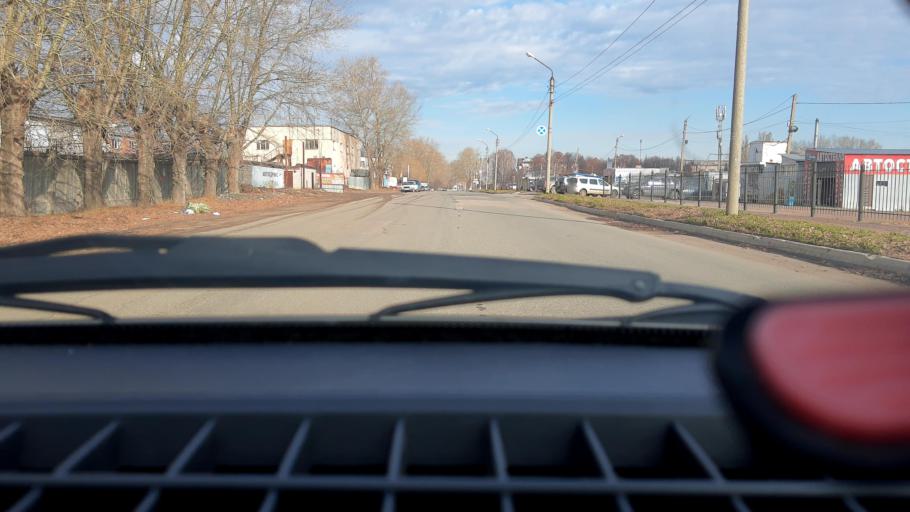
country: RU
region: Bashkortostan
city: Ufa
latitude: 54.8304
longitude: 56.0938
